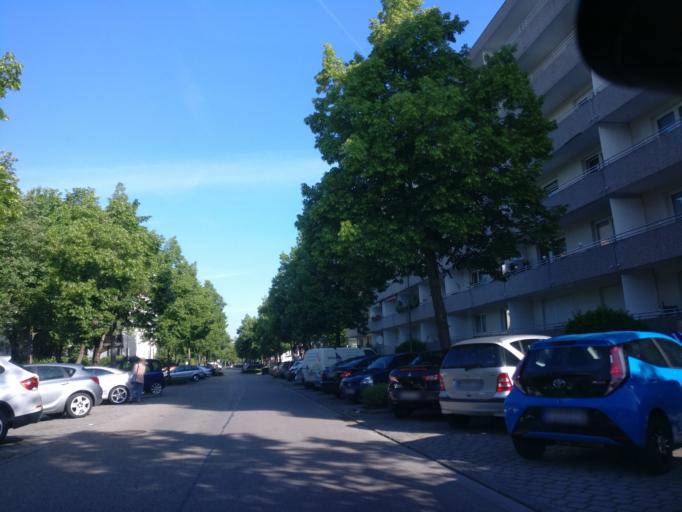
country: DE
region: Bavaria
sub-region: Upper Bavaria
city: Karlsfeld
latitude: 48.2276
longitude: 11.4670
